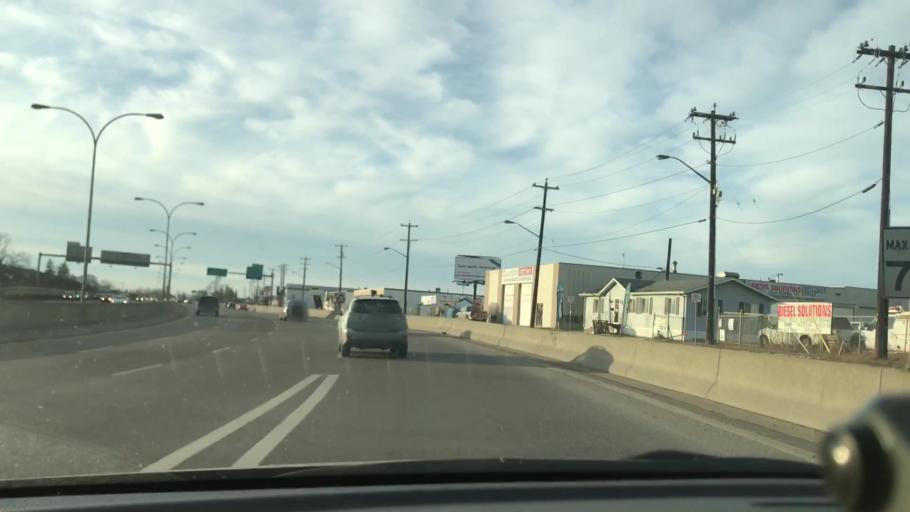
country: CA
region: Alberta
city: Edmonton
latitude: 53.5825
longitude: -113.4561
